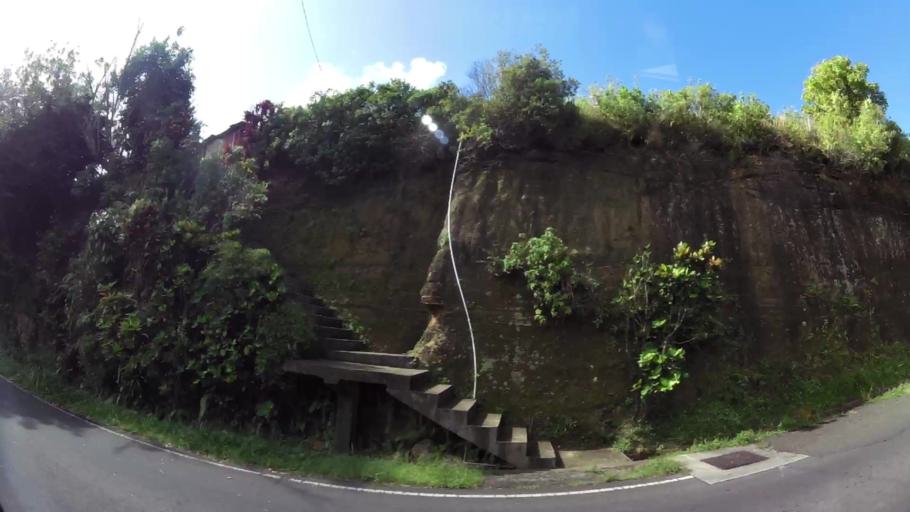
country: LC
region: Choiseul Quarter
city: Choiseul
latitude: 13.7936
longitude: -61.0380
